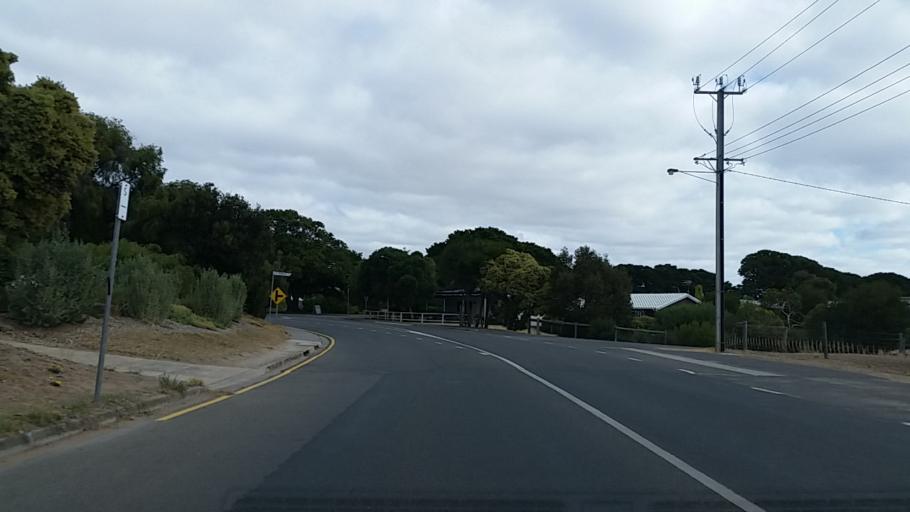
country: AU
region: South Australia
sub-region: Yankalilla
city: Normanville
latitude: -35.4439
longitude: 138.3163
